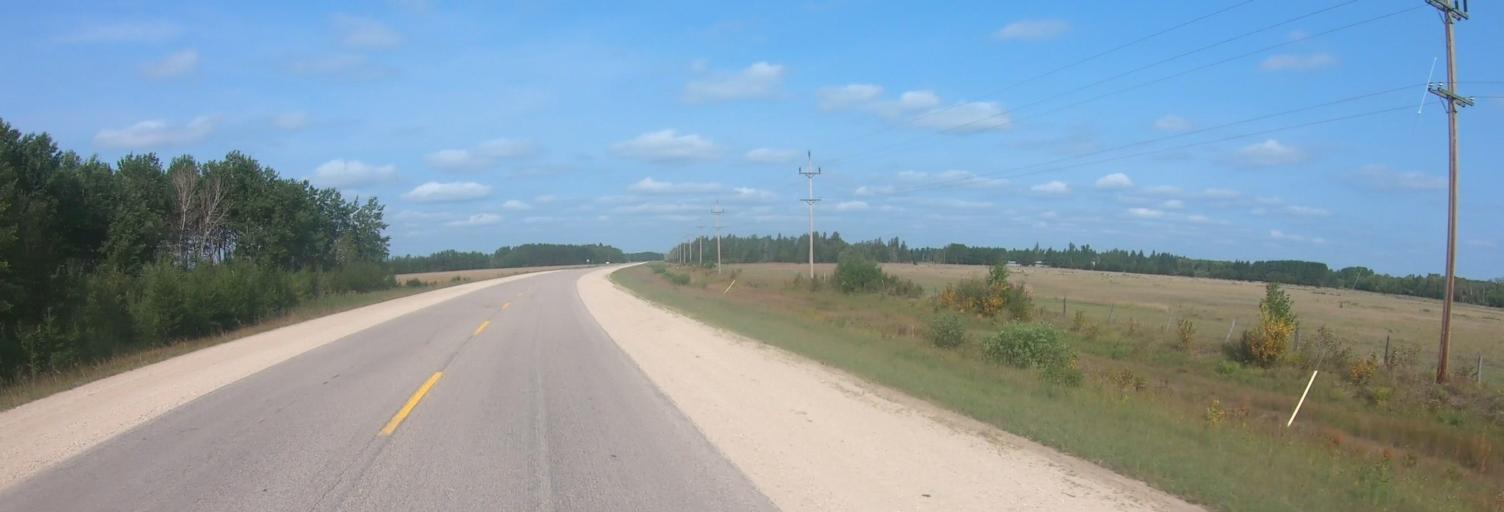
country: CA
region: Manitoba
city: La Broquerie
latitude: 49.1787
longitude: -96.2307
